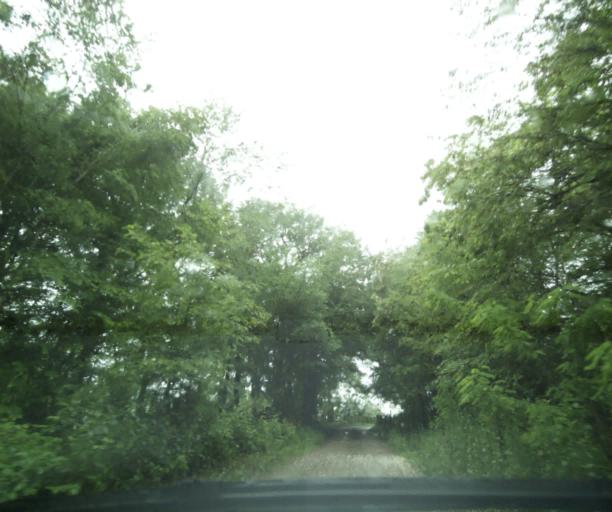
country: FR
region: Bourgogne
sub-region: Departement de Saone-et-Loire
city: Charolles
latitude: 46.3770
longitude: 4.3090
